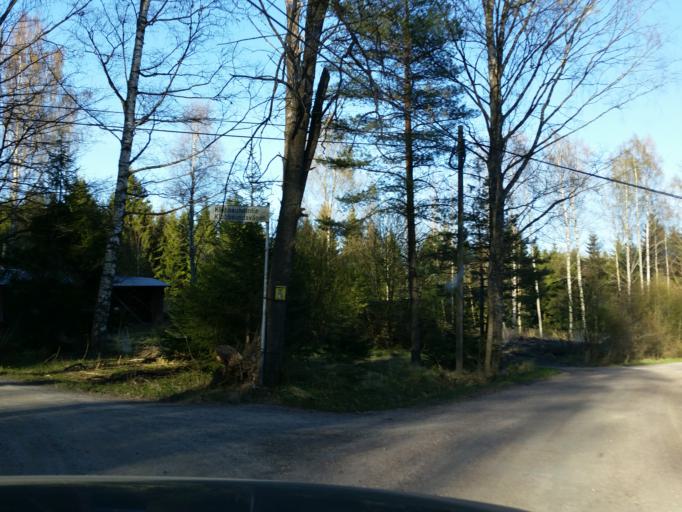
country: FI
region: Uusimaa
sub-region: Helsinki
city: Espoo
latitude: 60.1110
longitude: 24.6278
